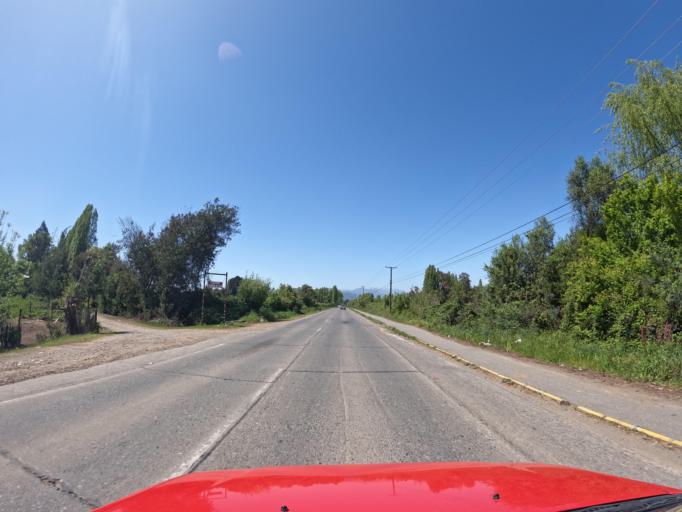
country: CL
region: Maule
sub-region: Provincia de Linares
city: Linares
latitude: -35.8285
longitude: -71.4988
